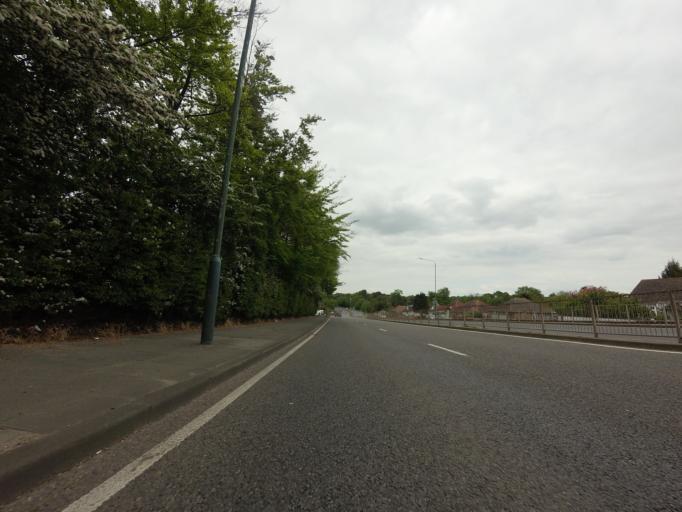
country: GB
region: England
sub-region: Greater London
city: Sidcup
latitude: 51.4172
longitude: 0.1295
